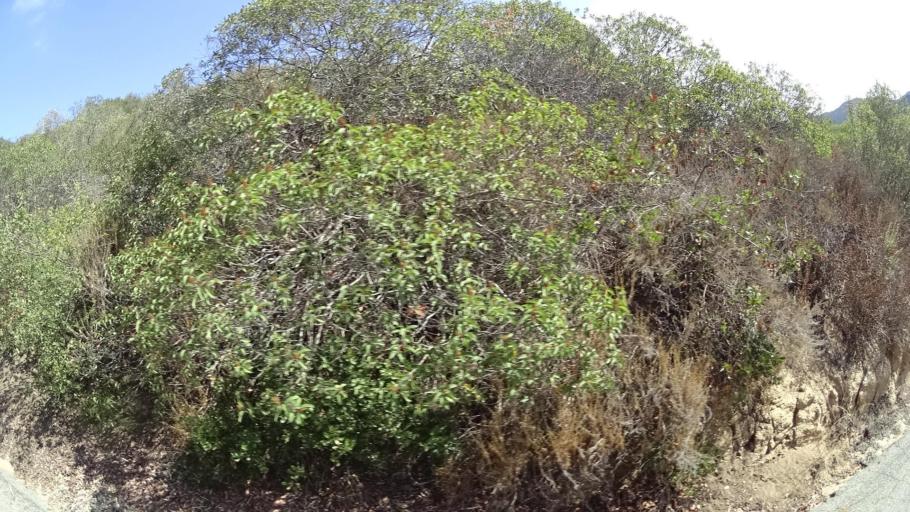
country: US
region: California
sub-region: San Diego County
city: Fallbrook
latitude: 33.4221
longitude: -117.3087
